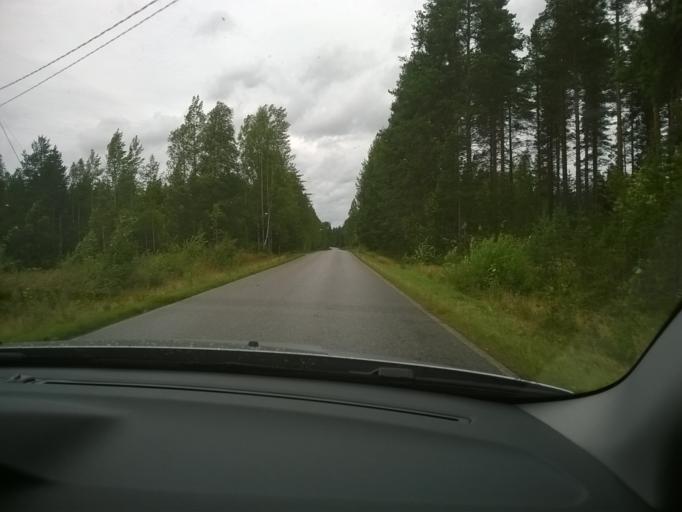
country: FI
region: Kainuu
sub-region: Kehys-Kainuu
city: Kuhmo
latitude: 64.1351
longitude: 29.4296
